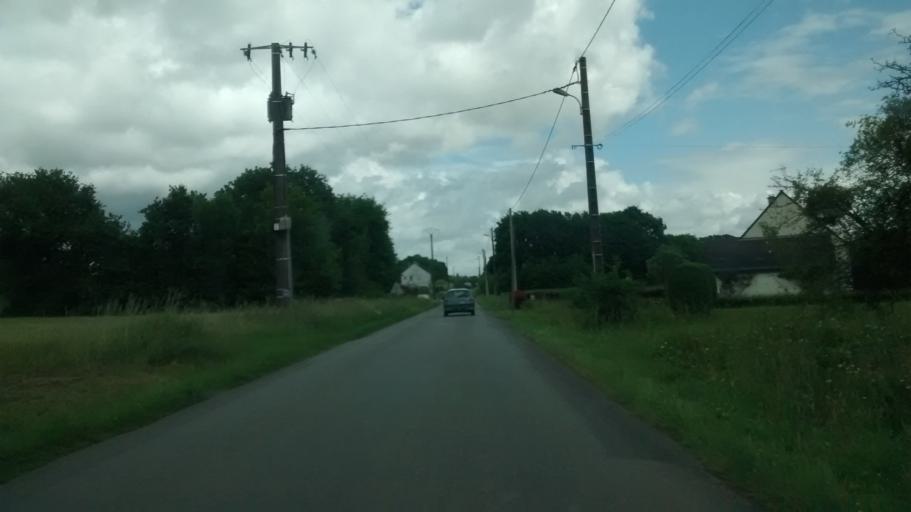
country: FR
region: Brittany
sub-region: Departement du Morbihan
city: La Gacilly
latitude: 47.7746
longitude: -2.1206
